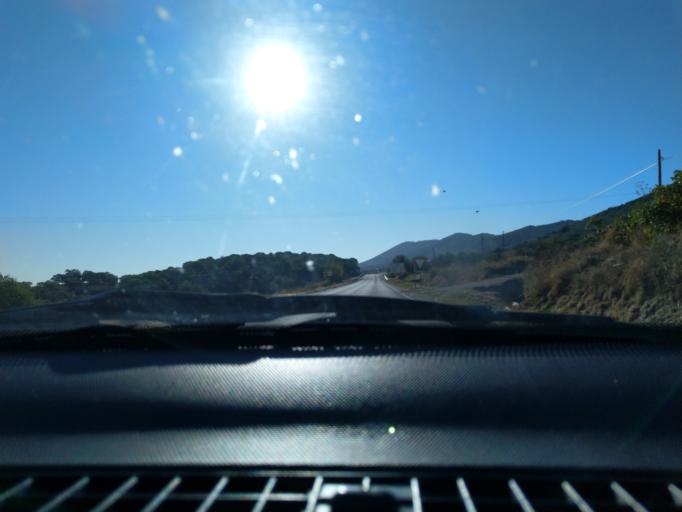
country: ES
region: Extremadura
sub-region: Provincia de Badajoz
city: Reina
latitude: 38.1482
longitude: -5.8915
